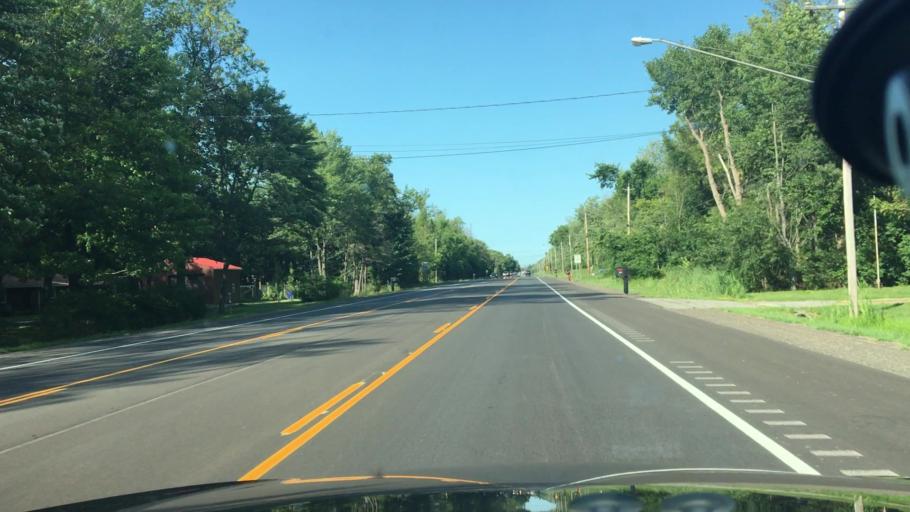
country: US
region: New York
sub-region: Erie County
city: Wanakah
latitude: 42.7160
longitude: -78.9065
